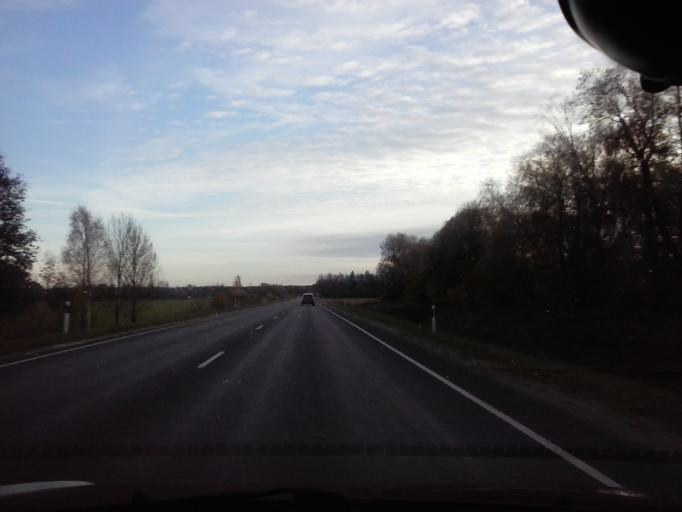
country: EE
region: Harju
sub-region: Nissi vald
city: Turba
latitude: 58.9104
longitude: 24.1110
